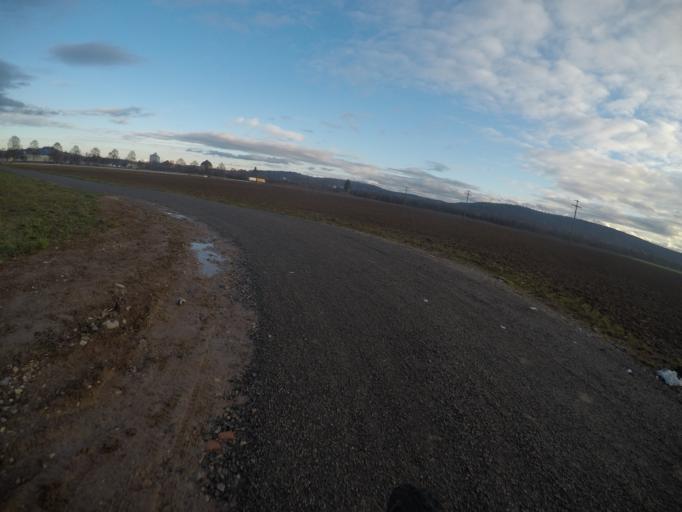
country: DE
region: Baden-Wuerttemberg
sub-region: Tuebingen Region
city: Tuebingen
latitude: 48.5075
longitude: 9.0358
